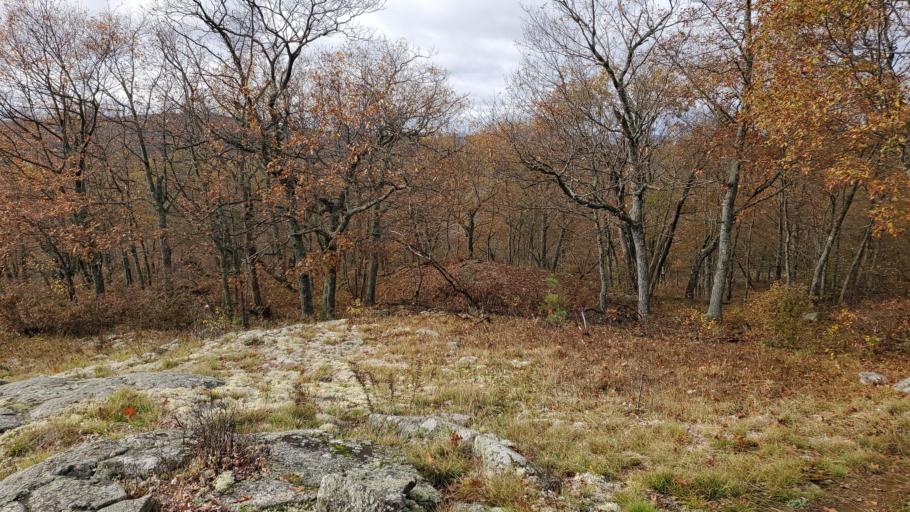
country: CA
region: Ontario
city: Renfrew
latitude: 45.2600
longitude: -77.1815
